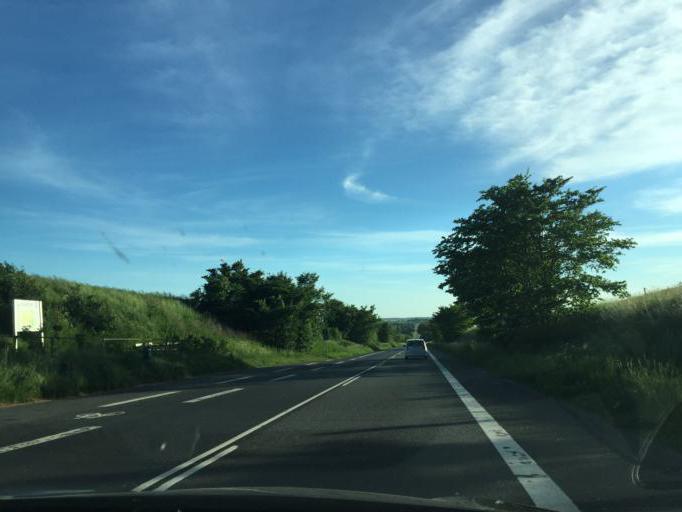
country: DK
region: Zealand
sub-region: Slagelse Kommune
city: Forlev
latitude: 55.3812
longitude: 11.3055
